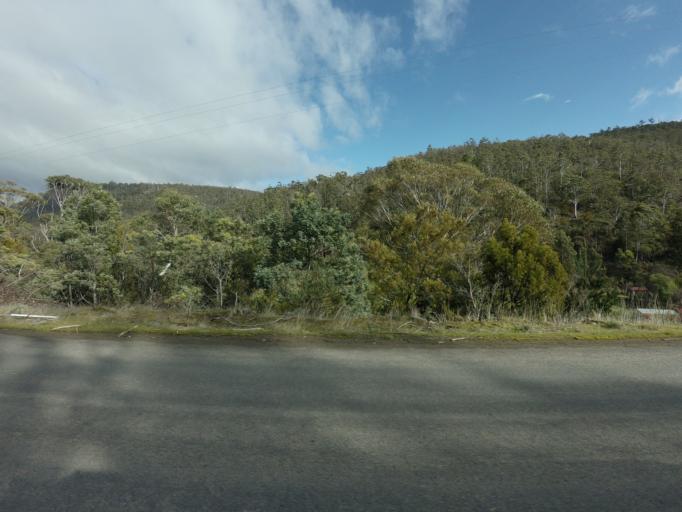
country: AU
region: Tasmania
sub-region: Derwent Valley
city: New Norfolk
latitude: -42.7875
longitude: 146.9468
